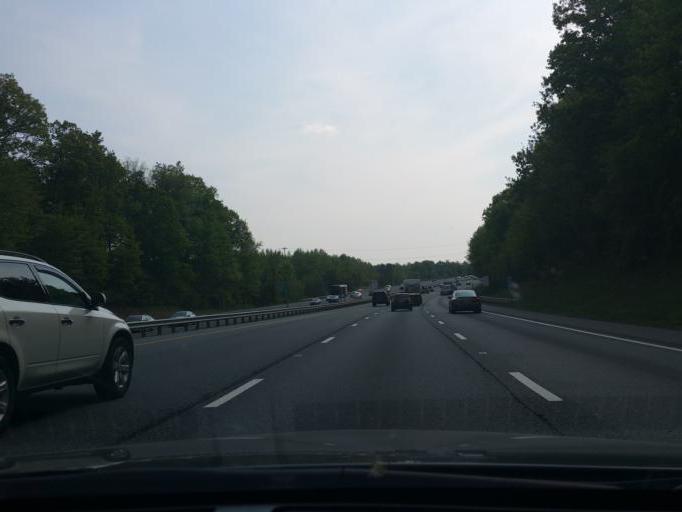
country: US
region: Maryland
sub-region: Harford County
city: Riverside
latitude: 39.4912
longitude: -76.2395
